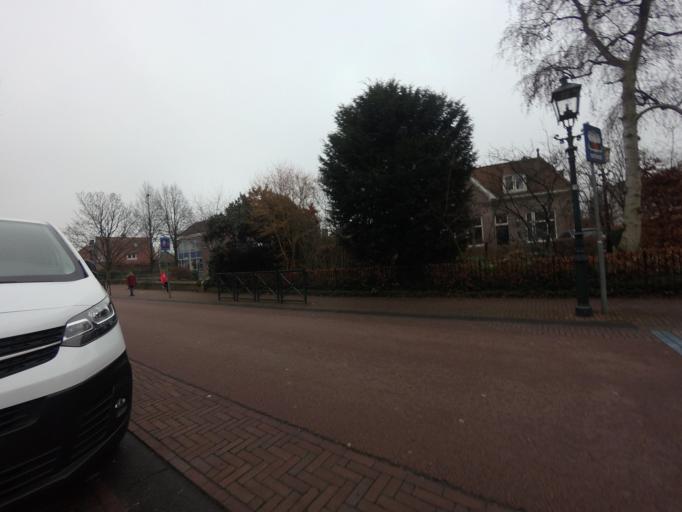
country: NL
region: Utrecht
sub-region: Gemeente Houten
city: Houten
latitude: 52.0267
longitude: 5.1636
